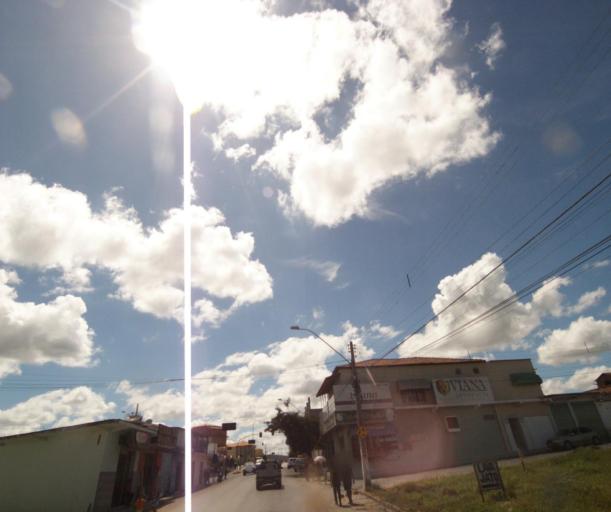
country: BR
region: Bahia
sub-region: Sao Felix Do Coribe
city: Santa Maria da Vitoria
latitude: -13.4036
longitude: -44.1947
